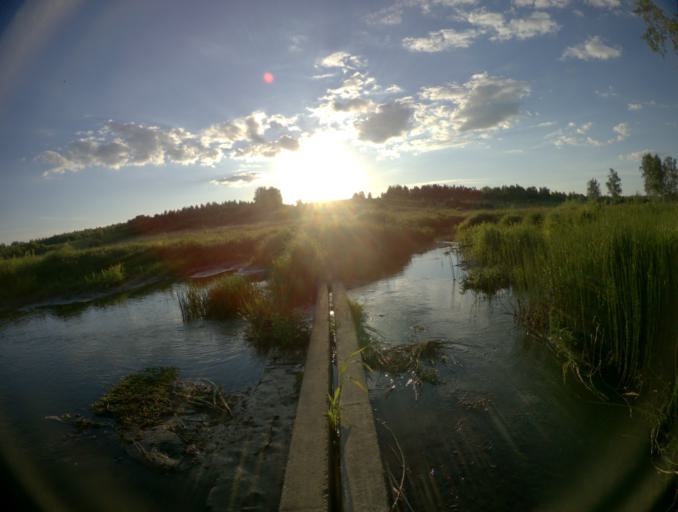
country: RU
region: Vladimir
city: Stavrovo
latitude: 56.2959
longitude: 39.9434
